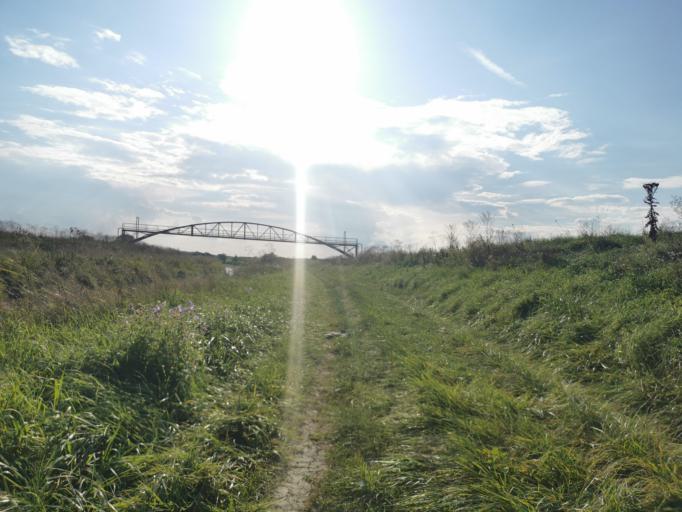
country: SK
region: Trnavsky
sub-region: Okres Senica
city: Senica
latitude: 48.6663
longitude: 17.2667
